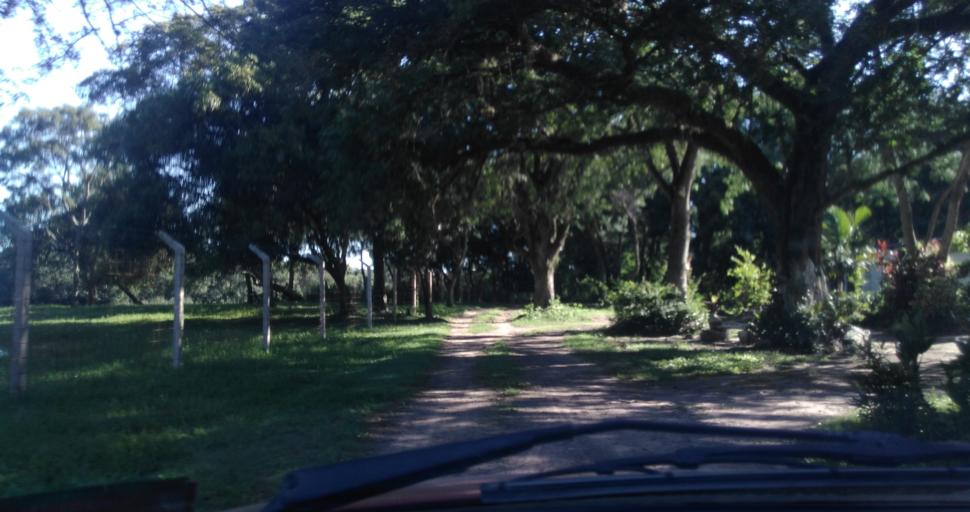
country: AR
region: Chaco
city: Resistencia
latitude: -27.4374
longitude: -58.9512
